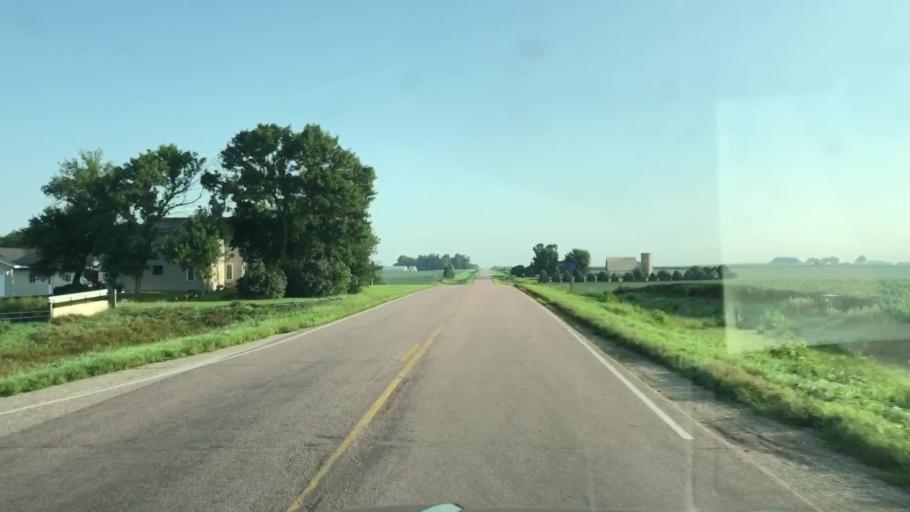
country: US
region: Iowa
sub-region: Lyon County
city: George
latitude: 43.2729
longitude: -95.9998
